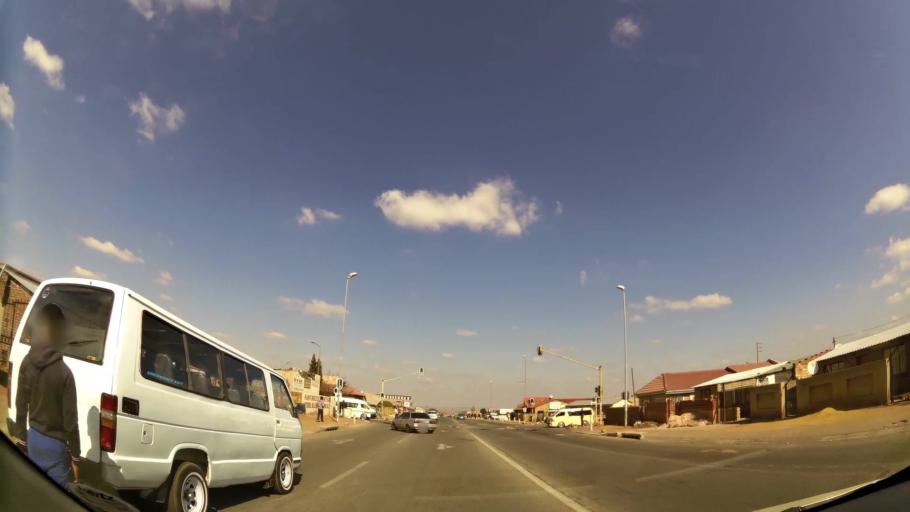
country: ZA
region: Gauteng
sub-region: West Rand District Municipality
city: Krugersdorp
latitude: -26.1608
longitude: 27.7817
